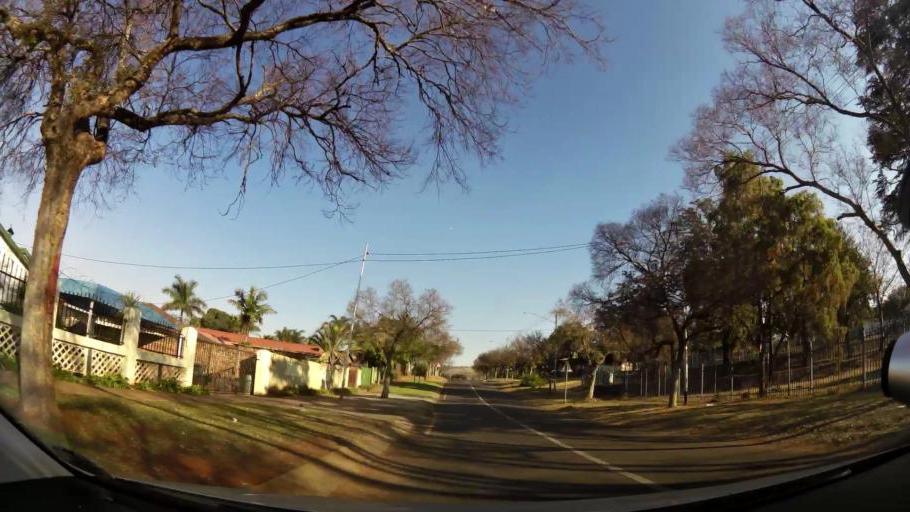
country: ZA
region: Gauteng
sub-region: City of Tshwane Metropolitan Municipality
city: Pretoria
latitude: -25.7534
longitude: 28.1409
